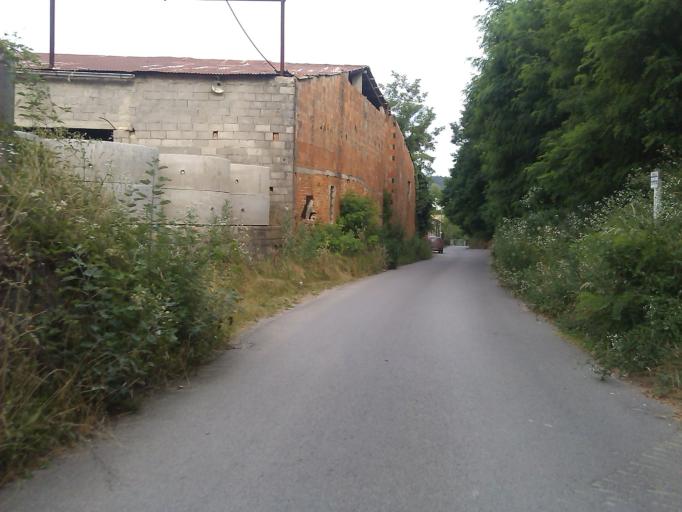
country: IT
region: Tuscany
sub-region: Province of Arezzo
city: Bucine
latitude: 43.4970
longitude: 11.6307
